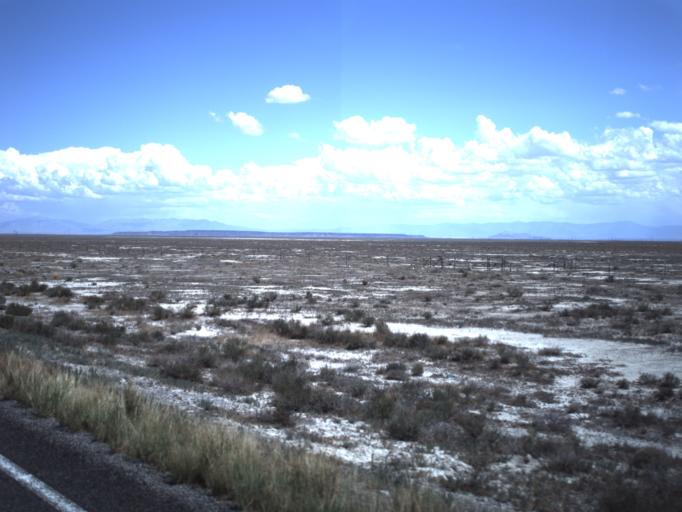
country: US
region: Utah
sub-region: Millard County
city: Delta
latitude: 39.1967
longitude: -112.9895
